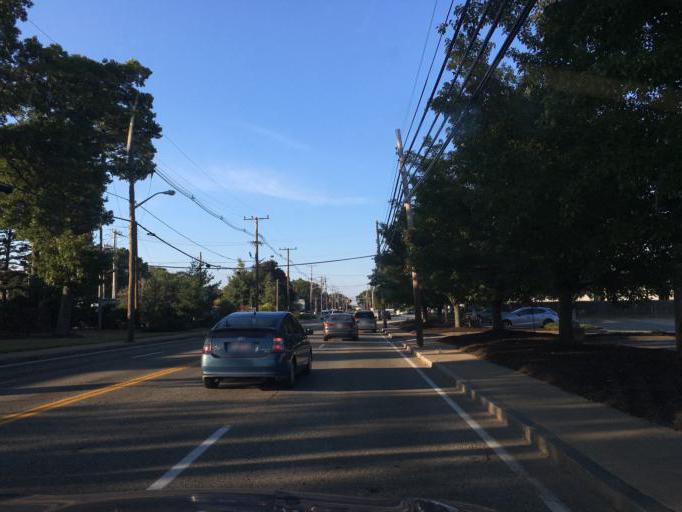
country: US
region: Rhode Island
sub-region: Kent County
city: Warwick
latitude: 41.7354
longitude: -71.4406
